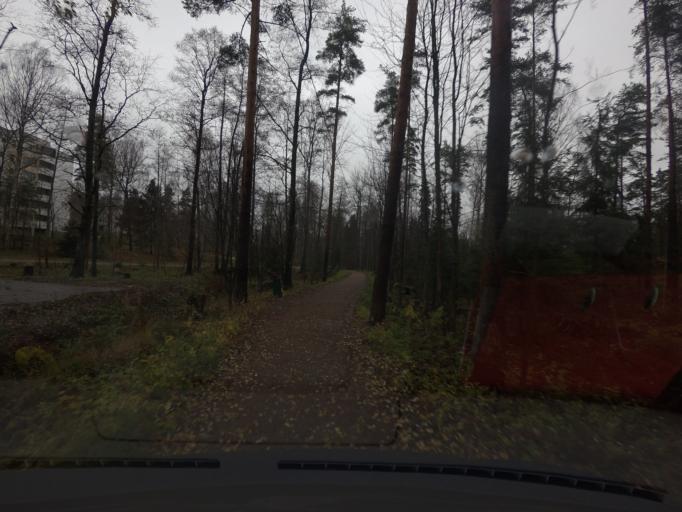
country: FI
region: Uusimaa
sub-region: Helsinki
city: Kauniainen
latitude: 60.2287
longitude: 24.7510
